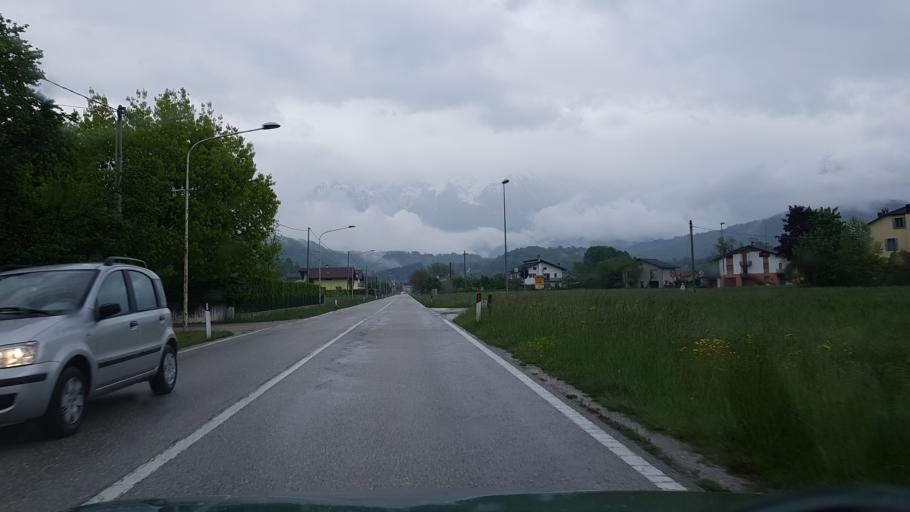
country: IT
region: Veneto
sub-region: Provincia di Belluno
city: Puos d'Alpago
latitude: 46.1361
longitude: 12.3493
